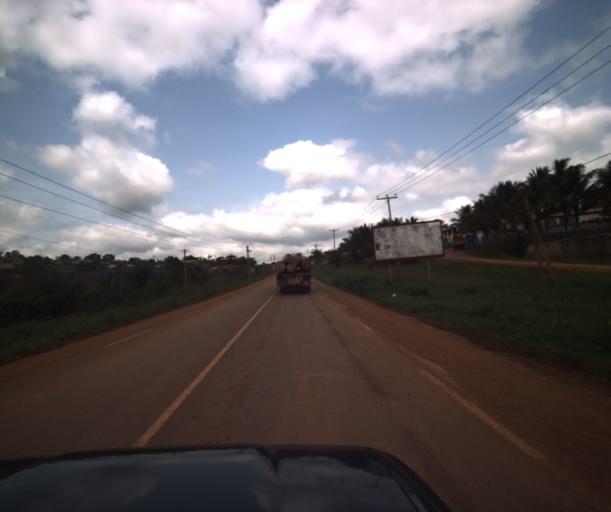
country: CM
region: Centre
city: Yaounde
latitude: 3.7948
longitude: 11.4813
